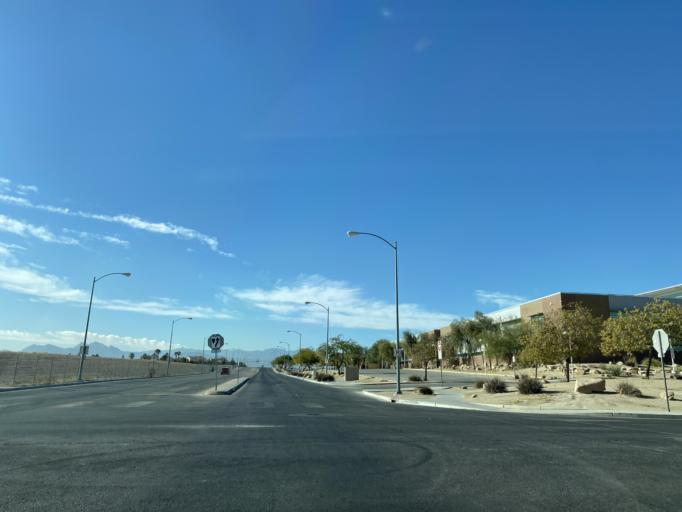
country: US
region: Nevada
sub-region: Clark County
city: North Las Vegas
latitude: 36.2838
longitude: -115.1393
